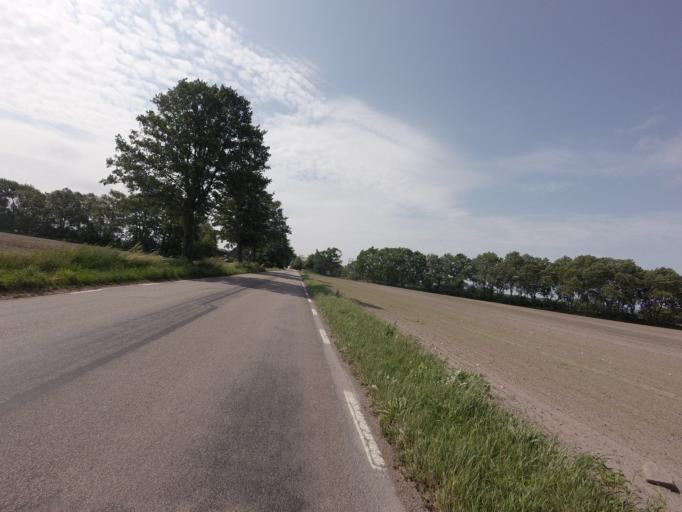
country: SE
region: Skane
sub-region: Helsingborg
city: Odakra
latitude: 56.2046
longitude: 12.7040
